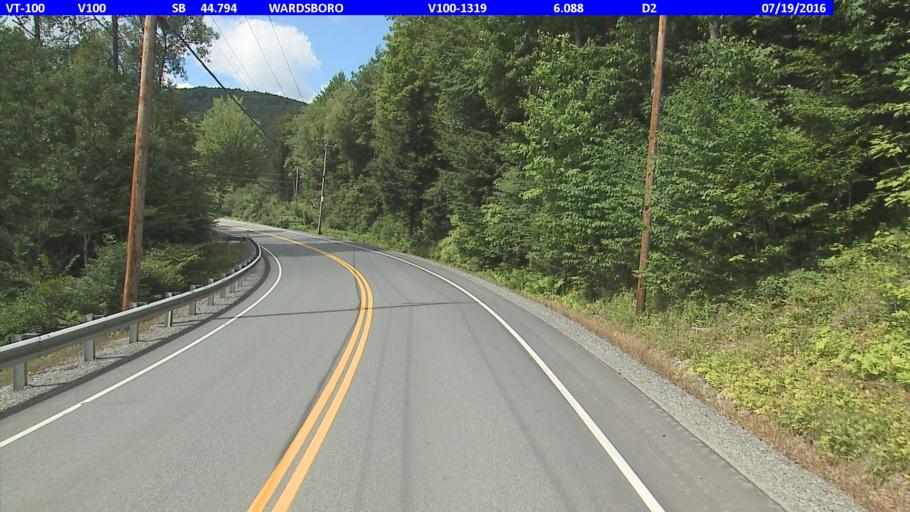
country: US
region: Vermont
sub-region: Windham County
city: Dover
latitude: 43.0865
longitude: -72.8665
